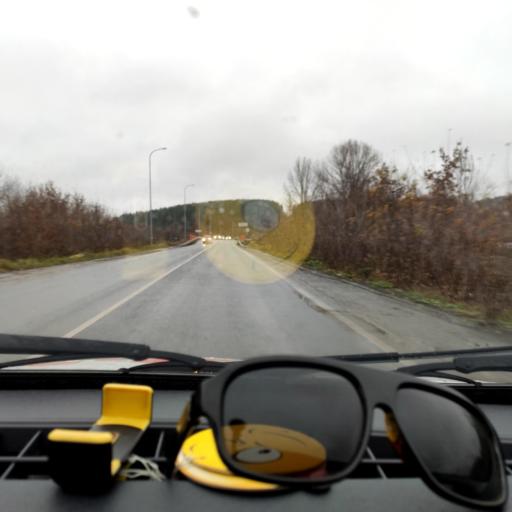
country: RU
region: Bashkortostan
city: Iglino
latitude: 54.8340
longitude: 56.3905
